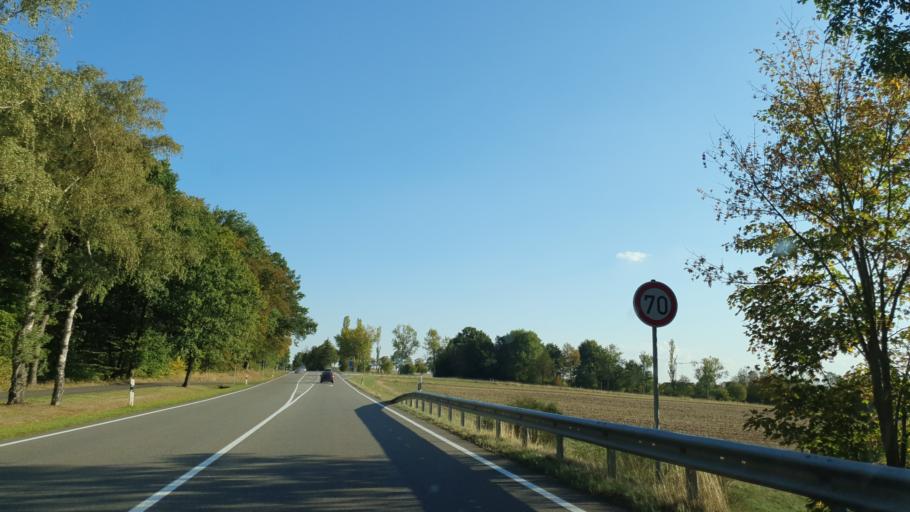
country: DE
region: Rheinland-Pfalz
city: Nortershausen
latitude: 50.2353
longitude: 7.5127
